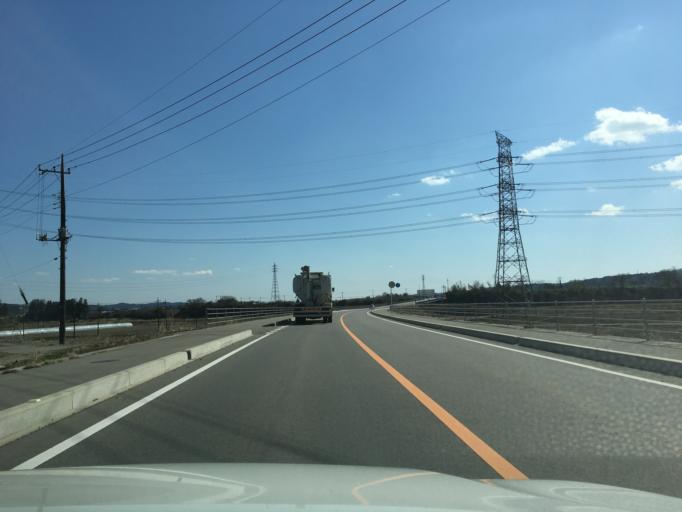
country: JP
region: Tochigi
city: Otawara
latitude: 36.7888
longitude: 140.1163
